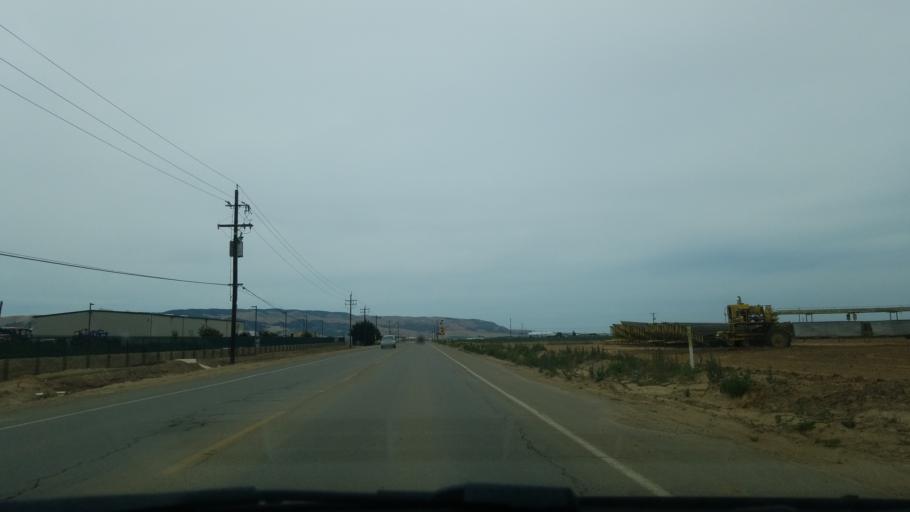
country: US
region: California
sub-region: Santa Barbara County
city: Santa Maria
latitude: 34.9210
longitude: -120.4856
